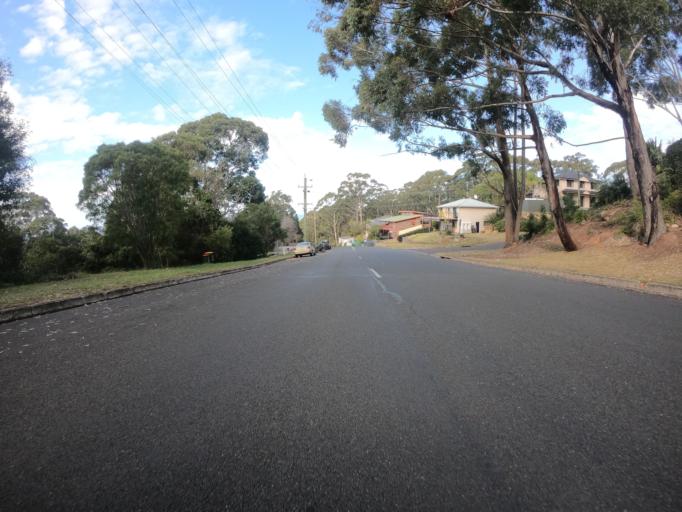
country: AU
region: New South Wales
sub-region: Wollongong
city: Bulli
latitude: -34.3345
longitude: 150.9042
